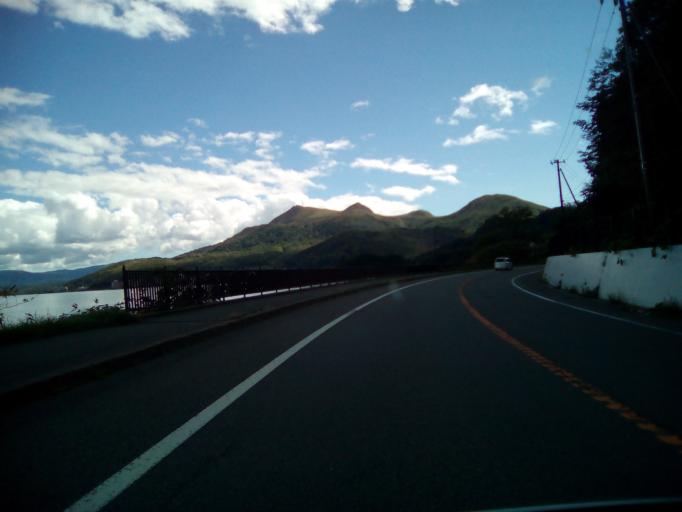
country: JP
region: Hokkaido
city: Date
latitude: 42.5780
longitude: 140.7977
